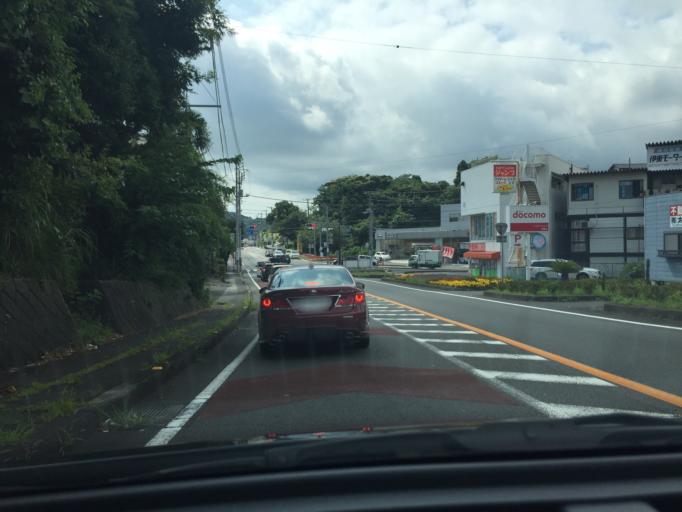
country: JP
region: Shizuoka
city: Ito
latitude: 34.9542
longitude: 139.1166
